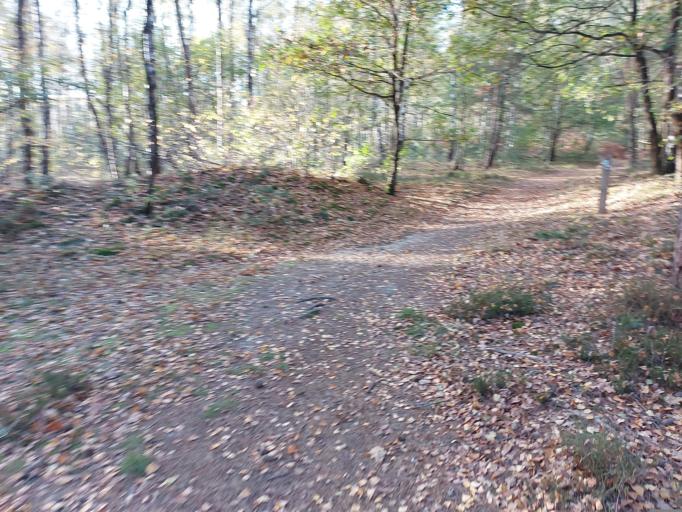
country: BE
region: Flanders
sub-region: Provincie Limburg
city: As
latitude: 51.0161
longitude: 5.5478
